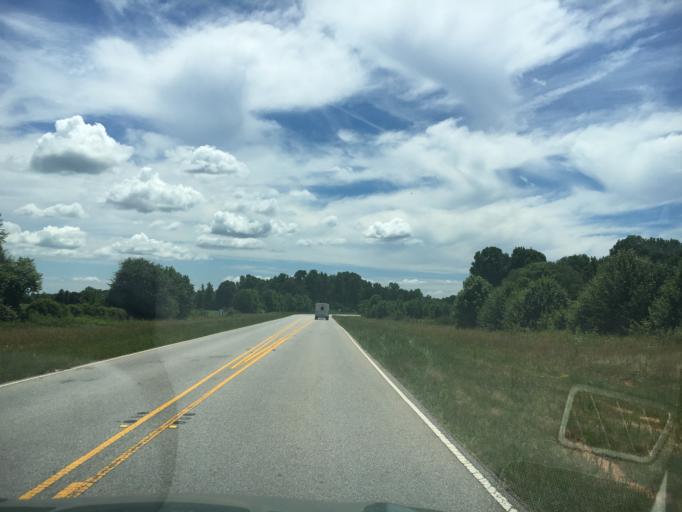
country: US
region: South Carolina
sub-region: Spartanburg County
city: Duncan
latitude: 34.8551
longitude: -82.1436
